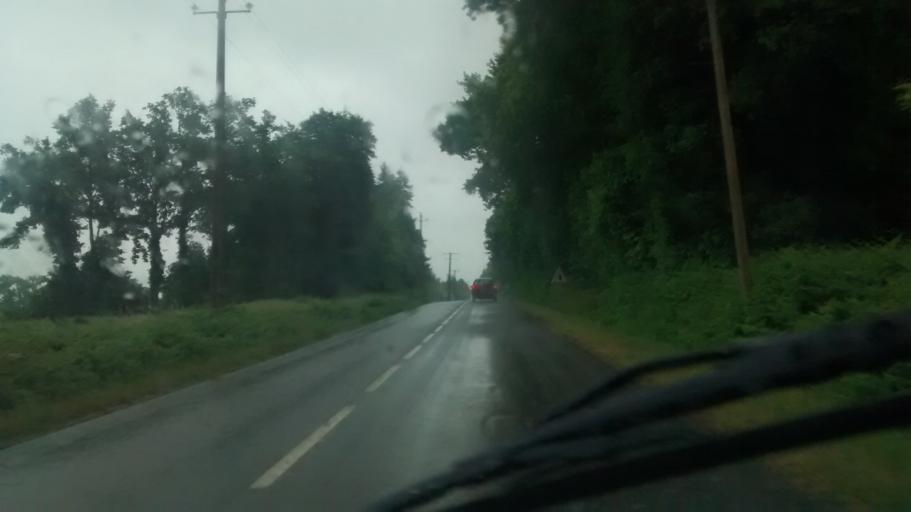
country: FR
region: Brittany
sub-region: Departement du Morbihan
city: La Gacilly
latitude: 47.7815
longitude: -2.1743
